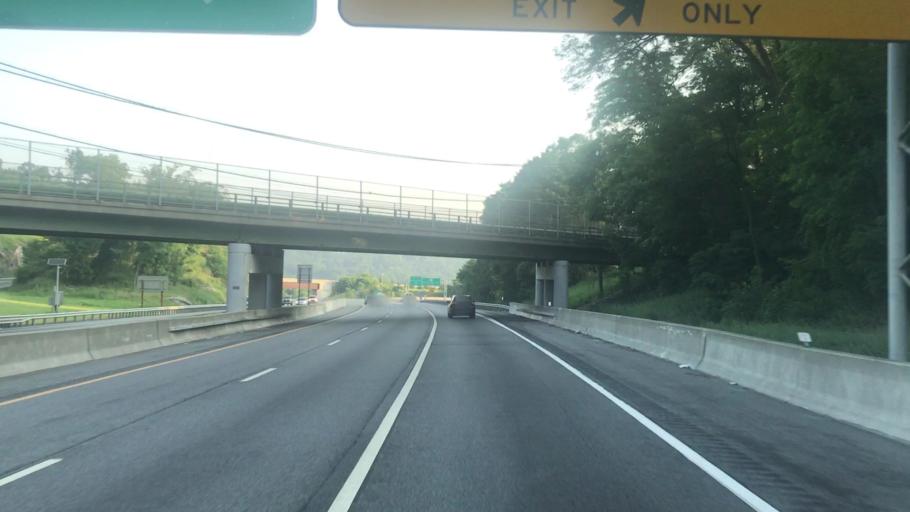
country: US
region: New York
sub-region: Westchester County
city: Elmsford
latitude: 41.0534
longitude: -73.8335
